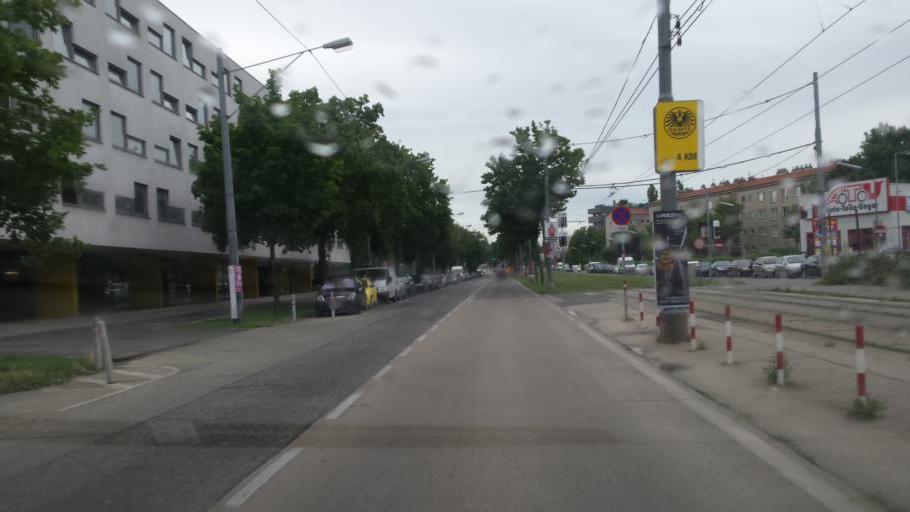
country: AT
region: Lower Austria
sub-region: Politischer Bezirk Wien-Umgebung
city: Schwechat
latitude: 48.1647
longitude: 16.4261
